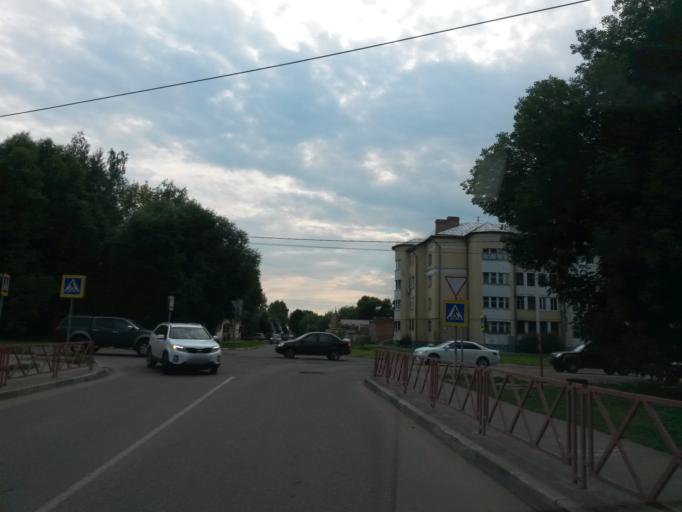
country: RU
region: Jaroslavl
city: Yaroslavl
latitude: 57.6055
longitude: 39.8163
